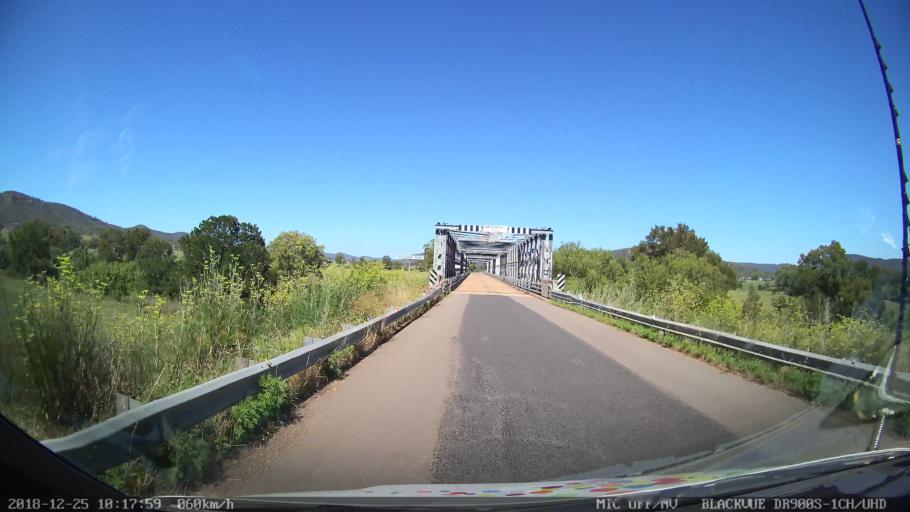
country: AU
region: New South Wales
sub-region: Muswellbrook
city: Denman
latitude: -32.3459
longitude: 150.5748
